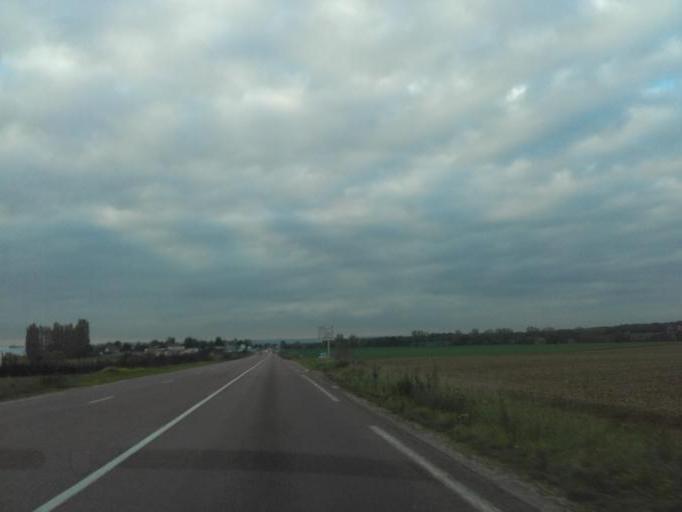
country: FR
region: Bourgogne
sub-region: Departement de Saone-et-Loire
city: Champforgeuil
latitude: 46.8382
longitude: 4.8178
